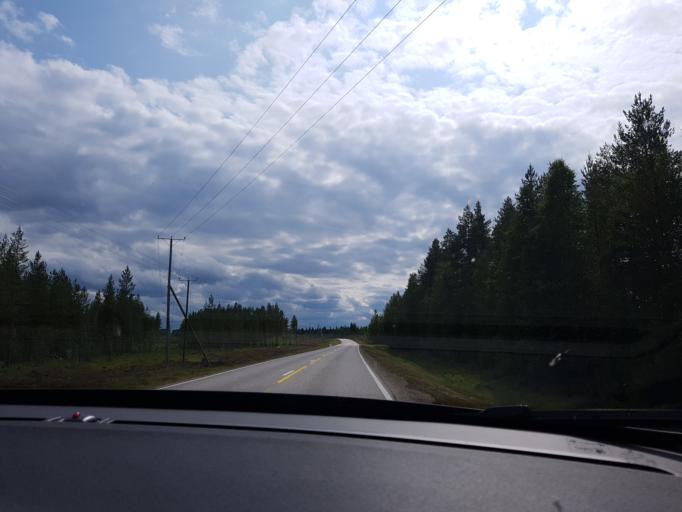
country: FI
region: Kainuu
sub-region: Kehys-Kainuu
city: Kuhmo
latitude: 64.3617
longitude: 29.8910
